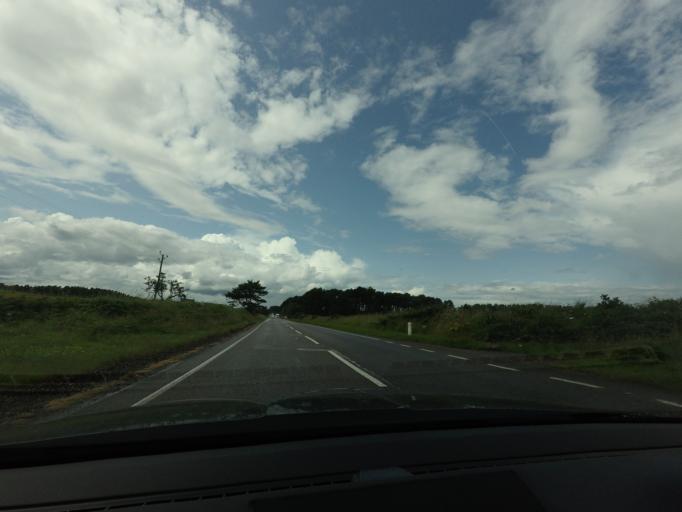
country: GB
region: Scotland
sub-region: Moray
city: Lhanbryd
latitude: 57.6309
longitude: -3.1760
